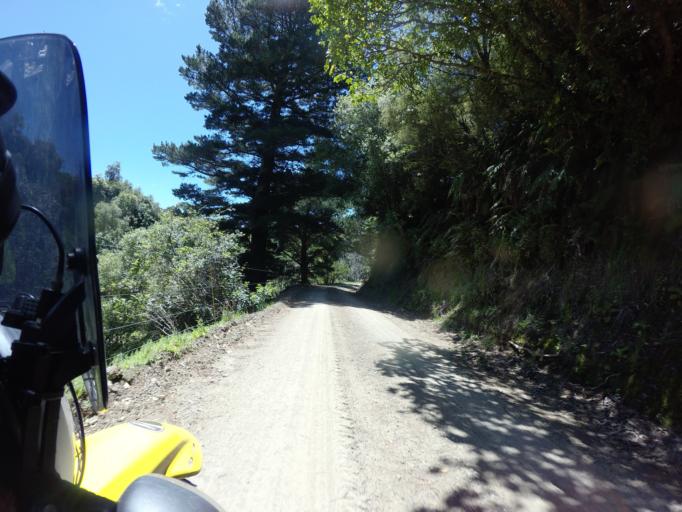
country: NZ
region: Bay of Plenty
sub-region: Opotiki District
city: Opotiki
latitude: -38.4041
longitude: 177.4529
